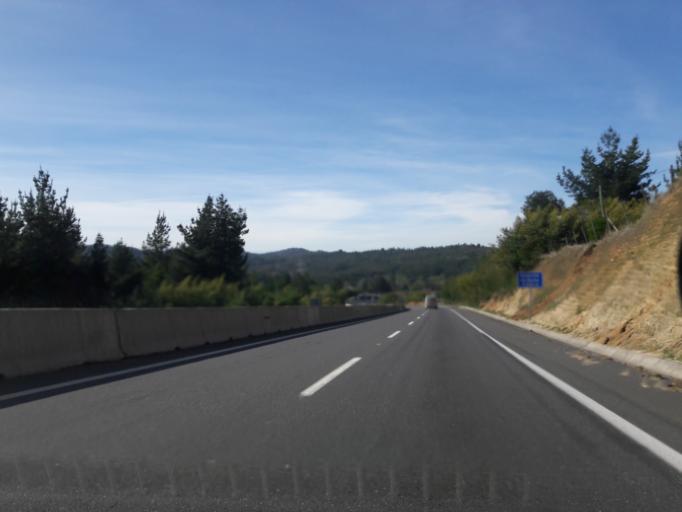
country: CL
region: Biobio
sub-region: Provincia de Biobio
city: Yumbel
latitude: -36.9777
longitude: -72.6449
